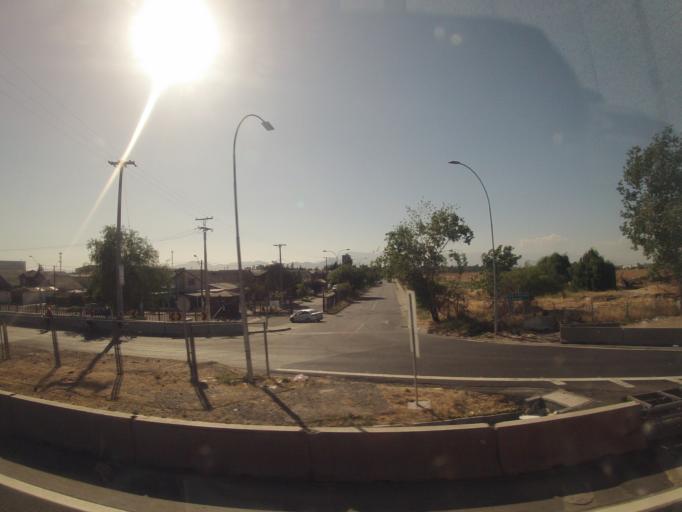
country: CL
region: Santiago Metropolitan
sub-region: Provincia de Santiago
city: Lo Prado
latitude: -33.5070
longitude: -70.6976
